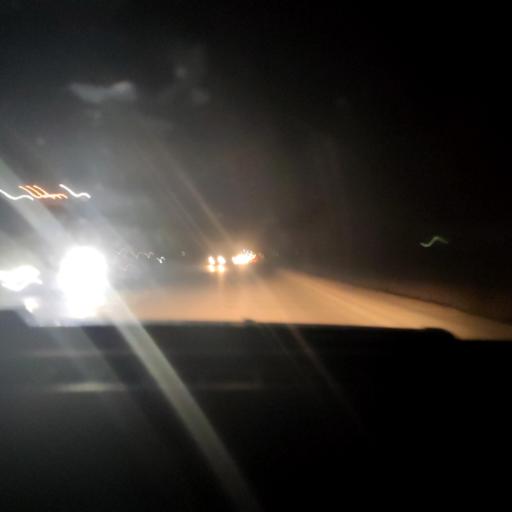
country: RU
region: Voronezj
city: Maslovka
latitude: 51.5238
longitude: 39.2969
